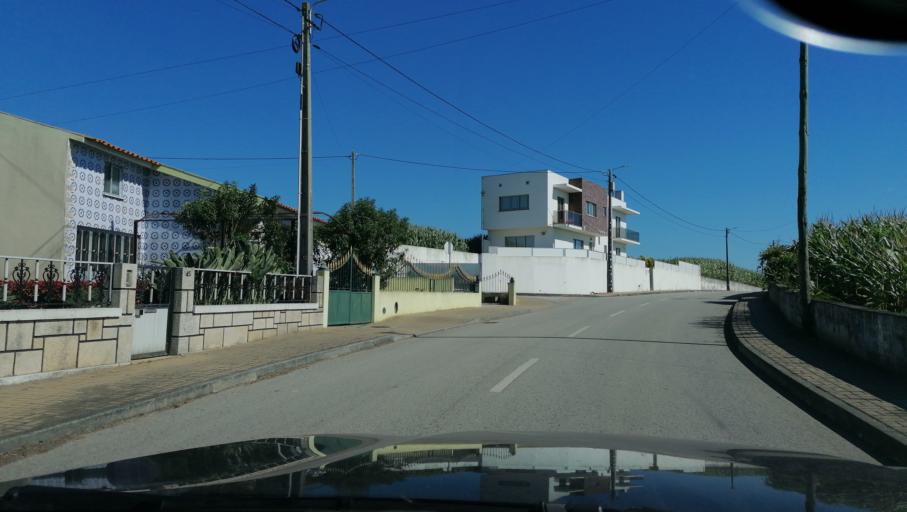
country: PT
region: Aveiro
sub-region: Estarreja
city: Salreu
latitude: 40.7451
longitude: -8.5466
